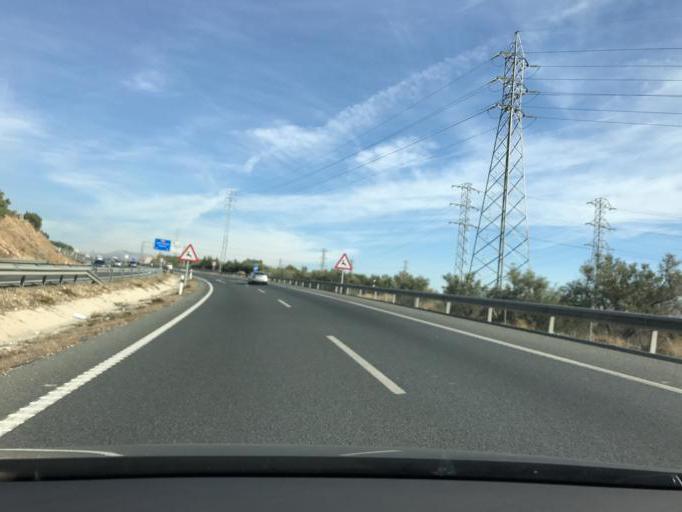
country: ES
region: Andalusia
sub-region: Provincia de Granada
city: Atarfe
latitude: 37.2265
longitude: -3.6957
